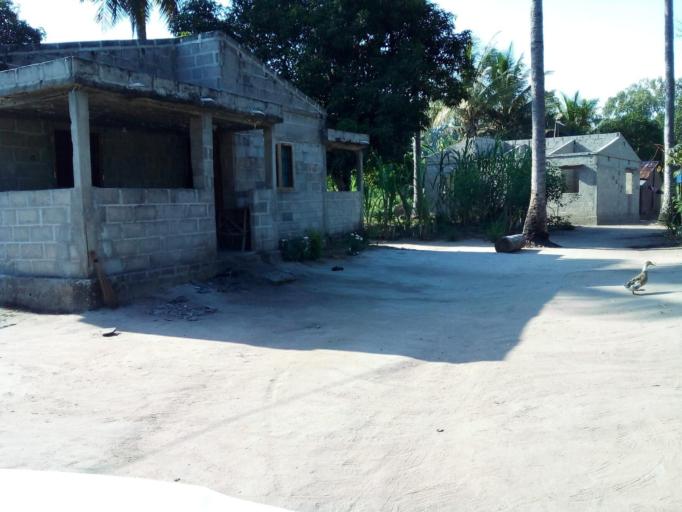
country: MZ
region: Zambezia
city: Quelimane
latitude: -17.6147
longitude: 36.8224
